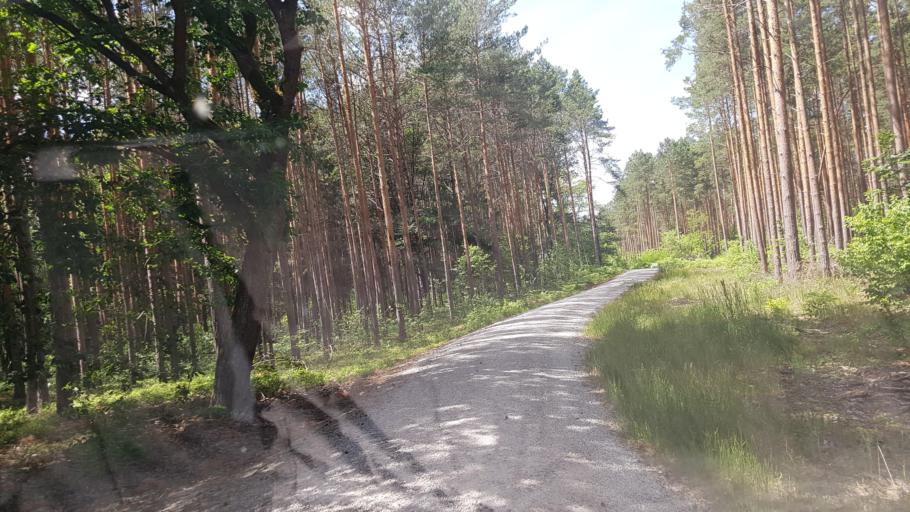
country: DE
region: Brandenburg
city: Plessa
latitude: 51.4952
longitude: 13.5957
